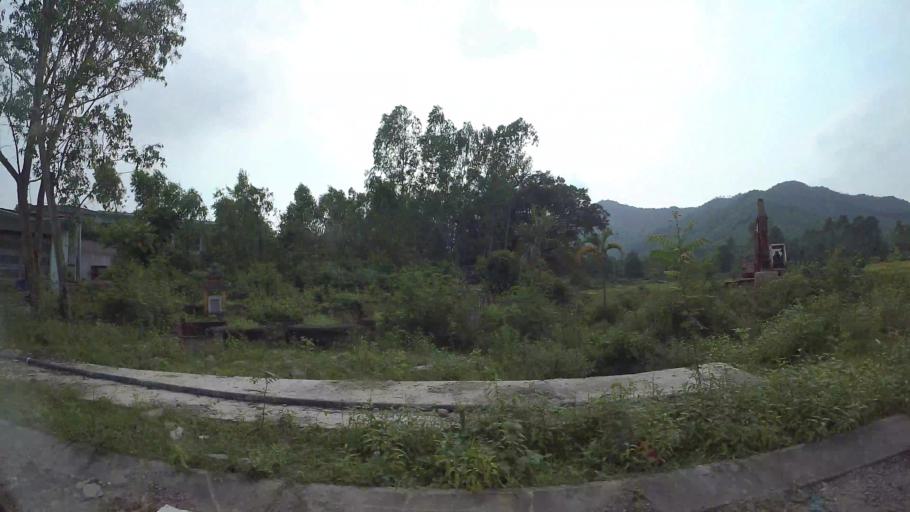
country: VN
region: Da Nang
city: Lien Chieu
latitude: 16.0501
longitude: 108.1458
